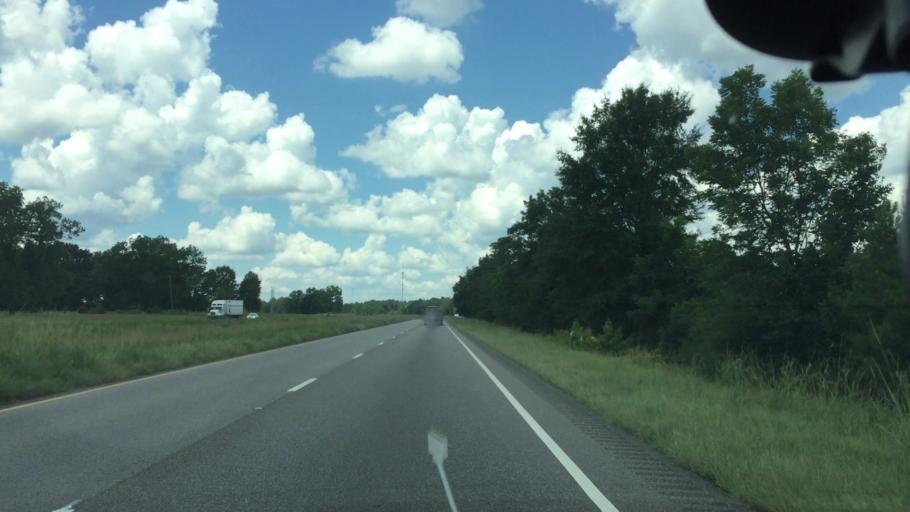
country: US
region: Alabama
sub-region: Montgomery County
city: Taylor
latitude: 32.0306
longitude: -86.0322
